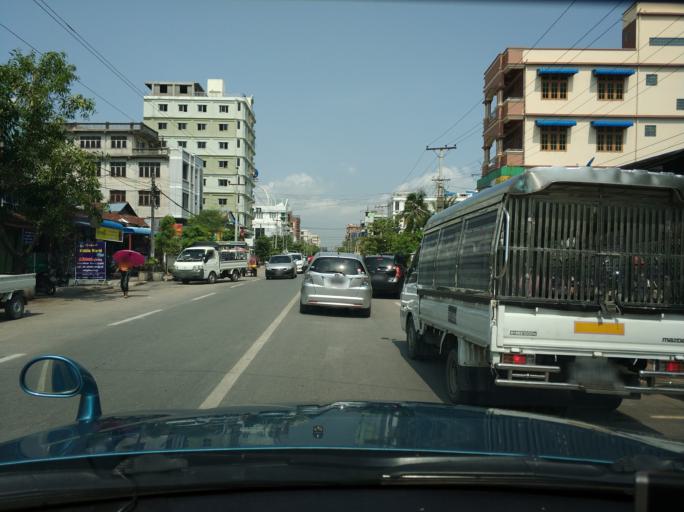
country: MM
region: Mandalay
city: Mandalay
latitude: 21.9658
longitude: 96.0923
